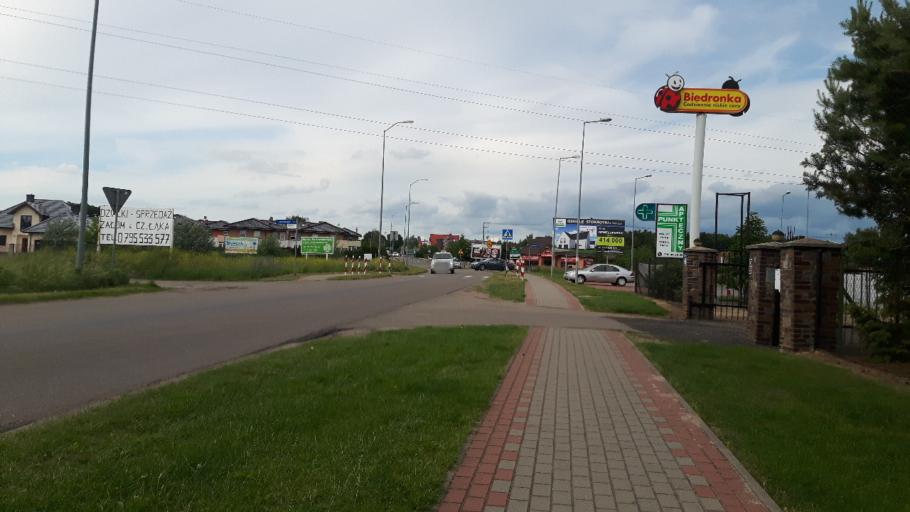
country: PL
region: West Pomeranian Voivodeship
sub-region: Powiat goleniowski
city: Goleniow
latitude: 53.4436
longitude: 14.7409
